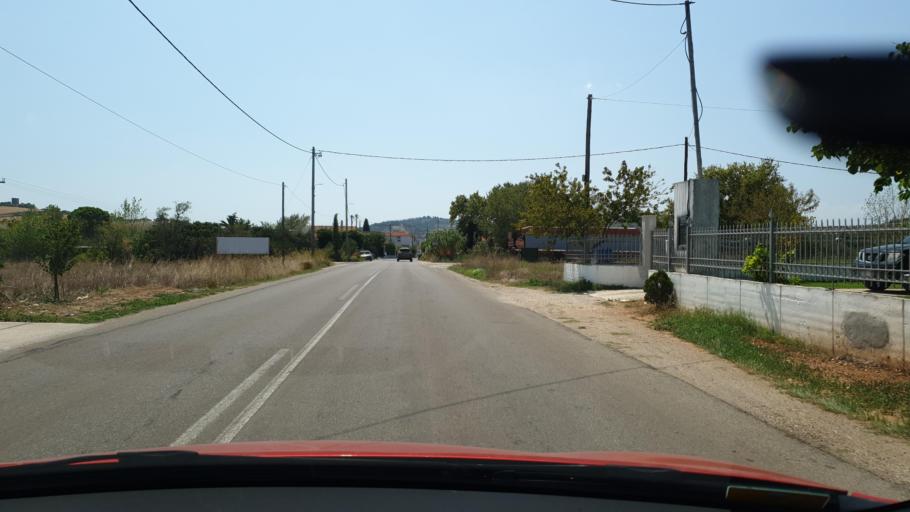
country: GR
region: Central Greece
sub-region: Nomos Evvoias
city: Aliveri
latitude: 38.4593
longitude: 24.1162
